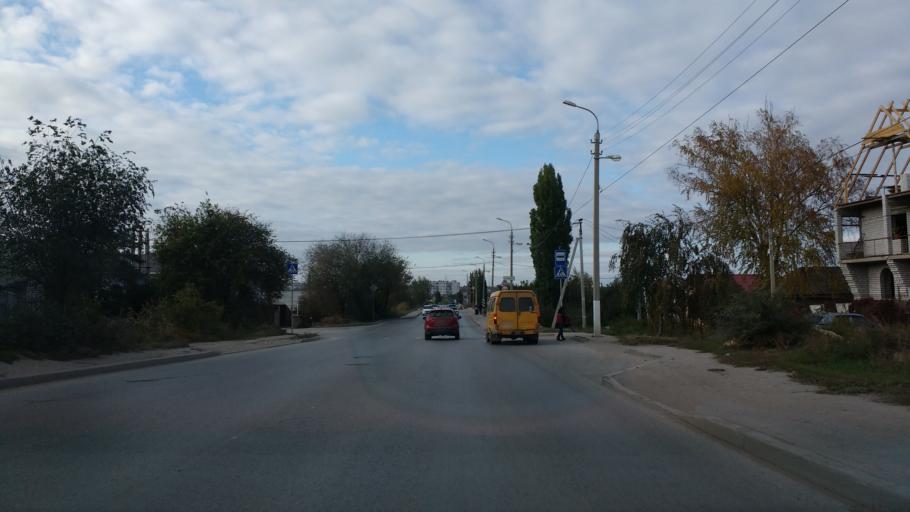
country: RU
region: Volgograd
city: Volgograd
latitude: 48.7682
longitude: 44.5273
